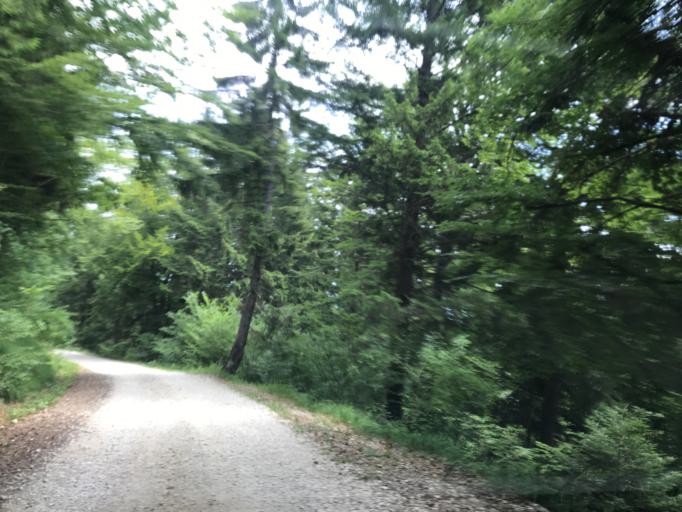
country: FR
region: Rhone-Alpes
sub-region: Departement de l'Isere
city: Saint-Vincent-de-Mercuze
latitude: 45.4117
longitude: 5.9406
